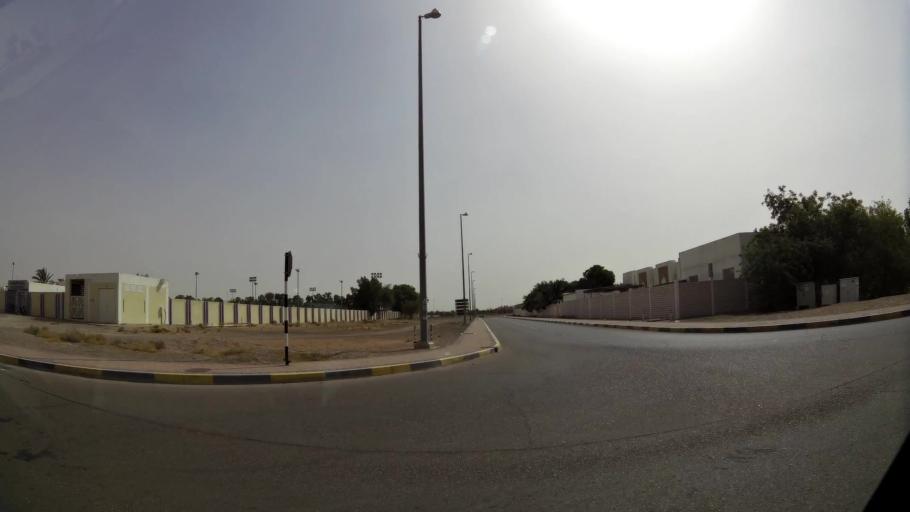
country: AE
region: Abu Dhabi
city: Al Ain
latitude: 24.1791
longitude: 55.6100
